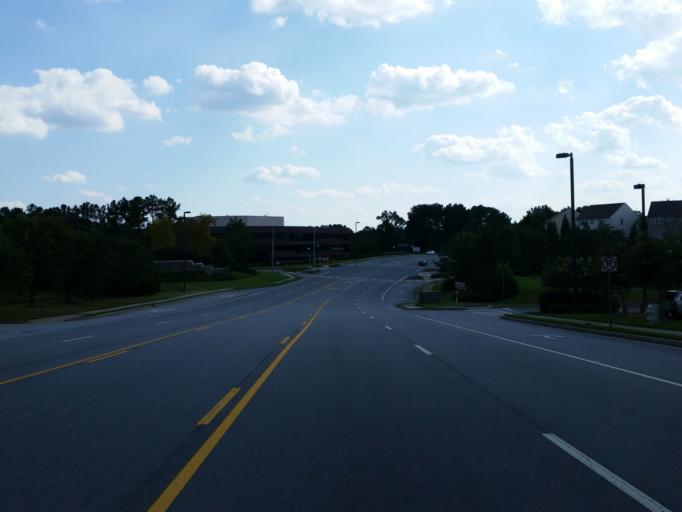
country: US
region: Georgia
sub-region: Gwinnett County
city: Duluth
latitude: 33.9566
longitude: -84.1119
